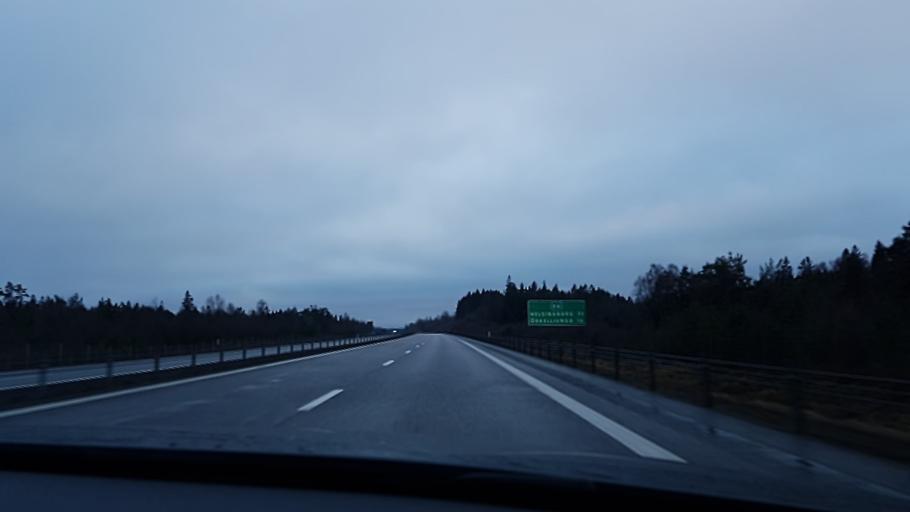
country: SE
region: Kronoberg
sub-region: Markaryds Kommun
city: Markaryd
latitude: 56.3545
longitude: 13.4705
